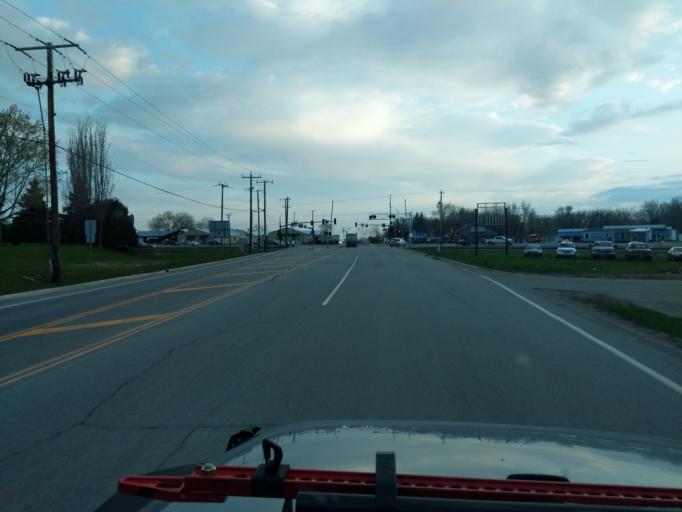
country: US
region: Minnesota
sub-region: Hennepin County
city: Rogers
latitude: 45.1682
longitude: -93.5214
